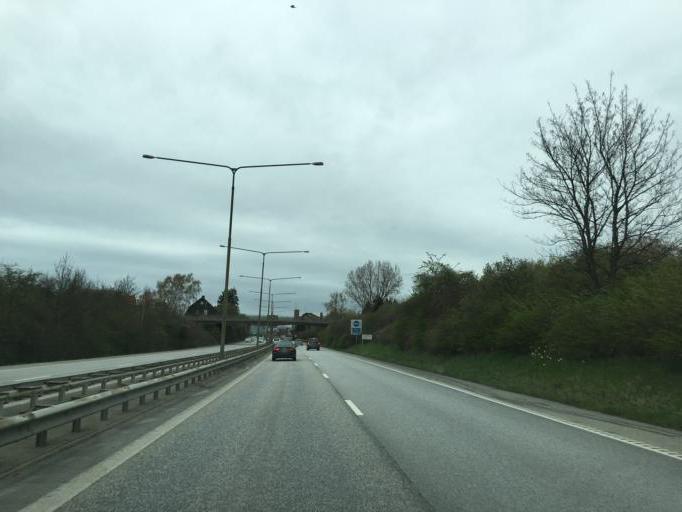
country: SE
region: Skane
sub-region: Malmo
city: Malmoe
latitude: 55.5733
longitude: 13.0048
